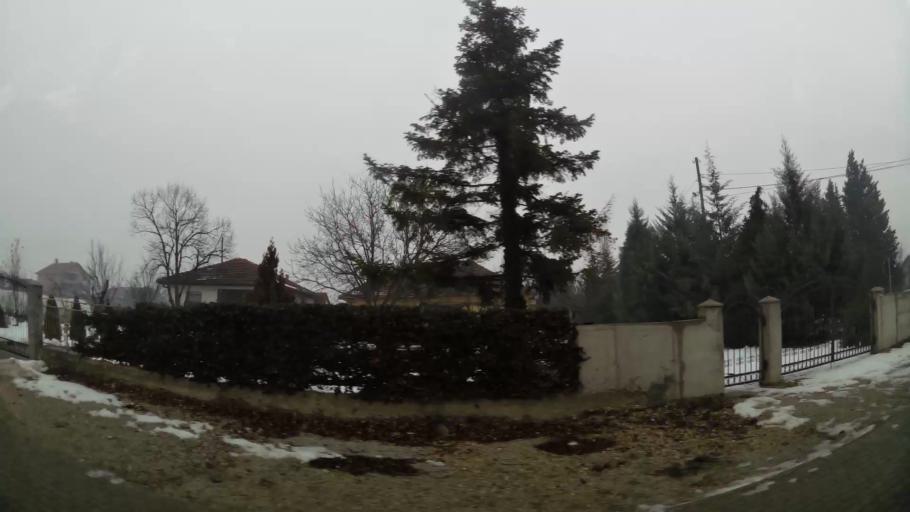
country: MK
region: Petrovec
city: Petrovec
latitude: 41.9288
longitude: 21.6273
